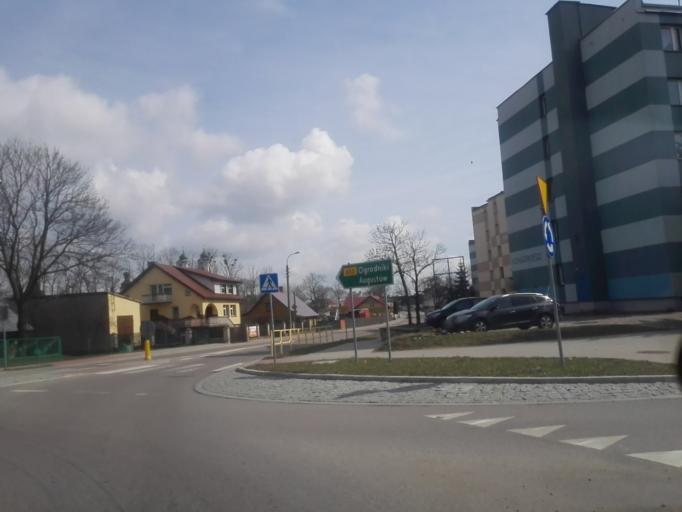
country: PL
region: Podlasie
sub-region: Powiat sejnenski
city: Sejny
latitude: 54.1079
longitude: 23.3408
